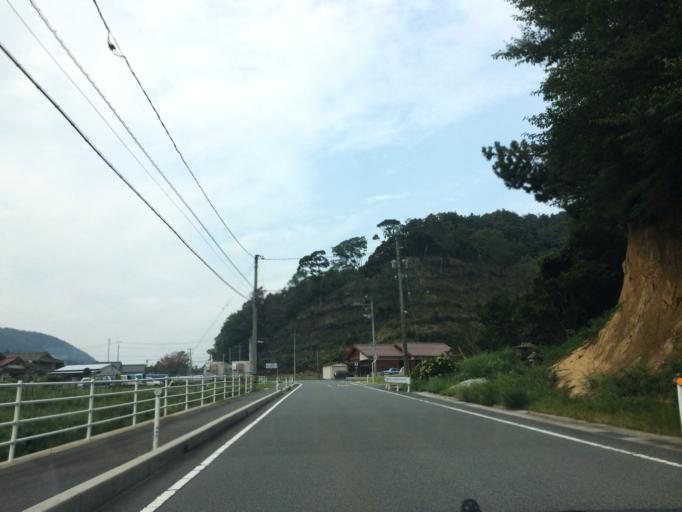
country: JP
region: Shimane
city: Odacho-oda
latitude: 35.1704
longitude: 132.6250
